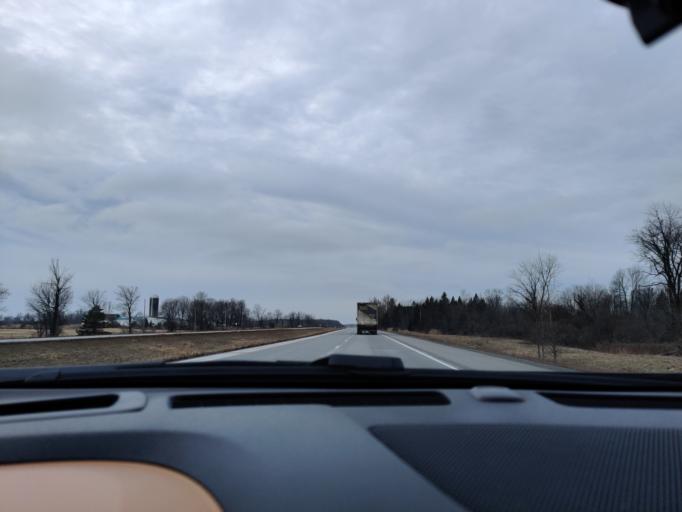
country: CA
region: Ontario
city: Cornwall
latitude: 45.1093
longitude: -74.5554
